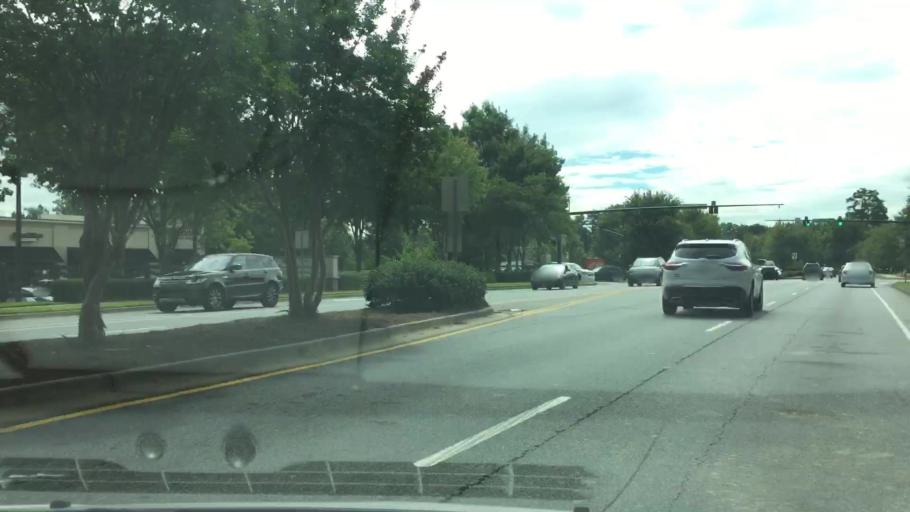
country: US
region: Georgia
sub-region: Fulton County
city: Alpharetta
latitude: 34.0910
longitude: -84.2758
